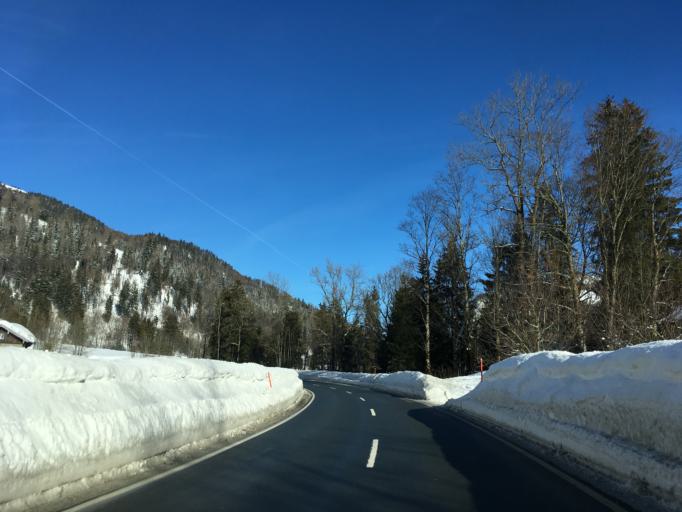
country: AT
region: Tyrol
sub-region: Politischer Bezirk Kufstein
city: Rettenschoss
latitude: 47.7149
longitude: 12.2862
